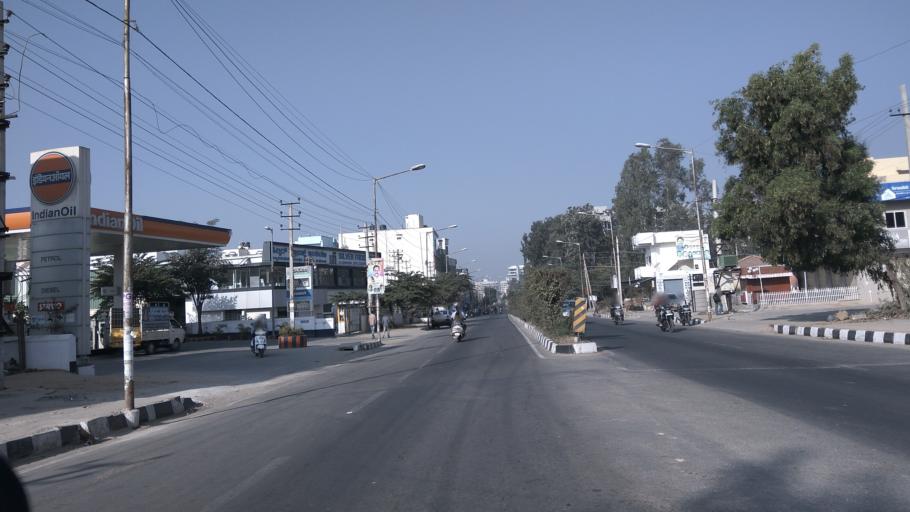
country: IN
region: Karnataka
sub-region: Bangalore Urban
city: Yelahanka
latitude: 13.1217
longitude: 77.6237
